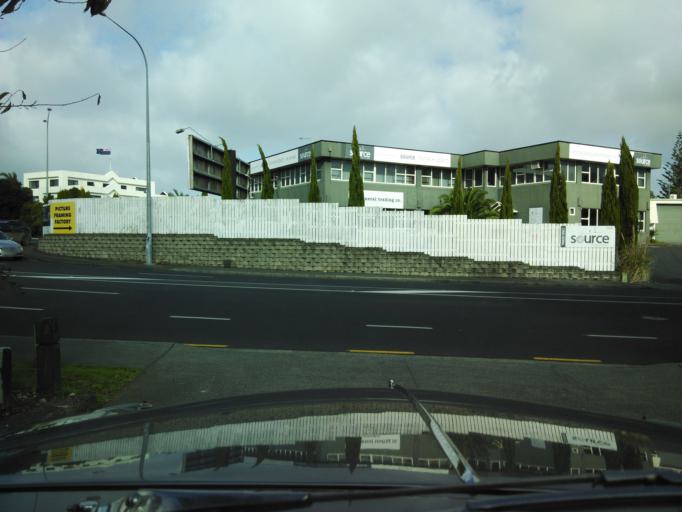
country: NZ
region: Auckland
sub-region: Auckland
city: Tamaki
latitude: -36.8994
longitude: 174.8153
